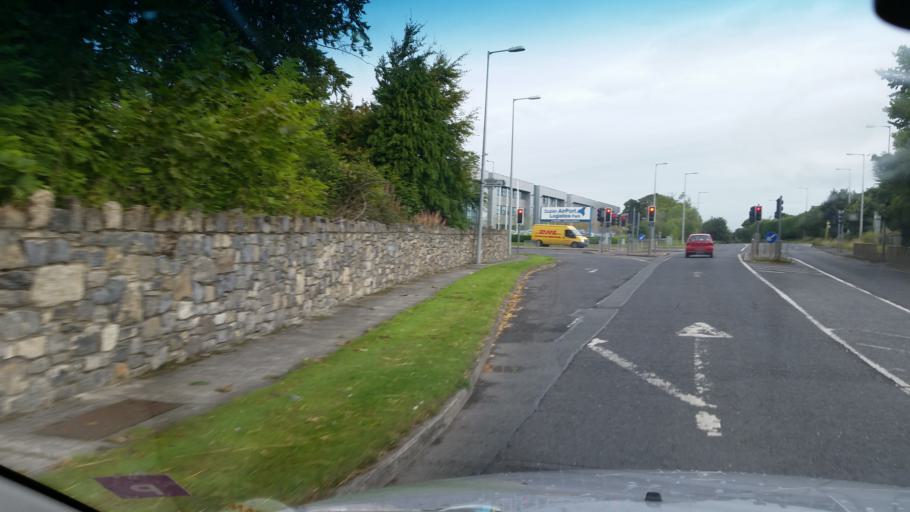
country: IE
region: Leinster
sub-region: Dublin City
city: Finglas
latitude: 53.4173
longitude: -6.3072
